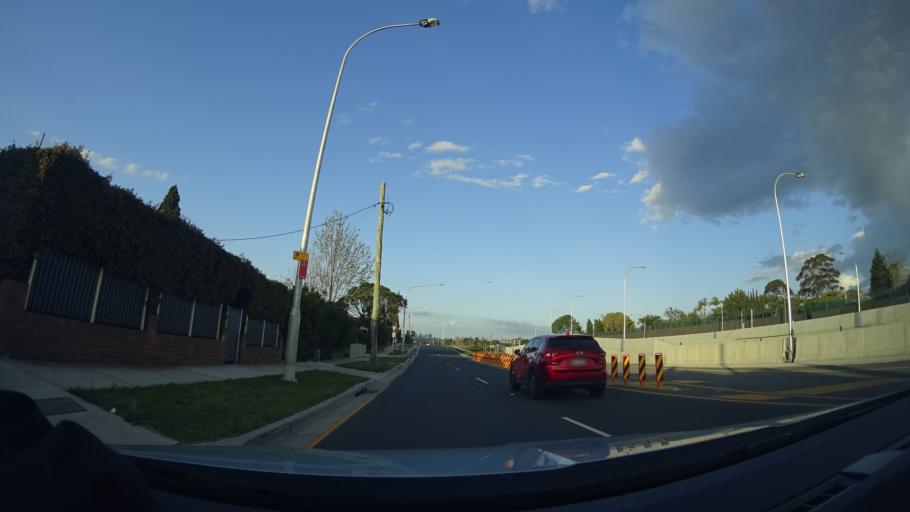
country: AU
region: New South Wales
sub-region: Ashfield
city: Ashfield
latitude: -33.8764
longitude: 151.1315
